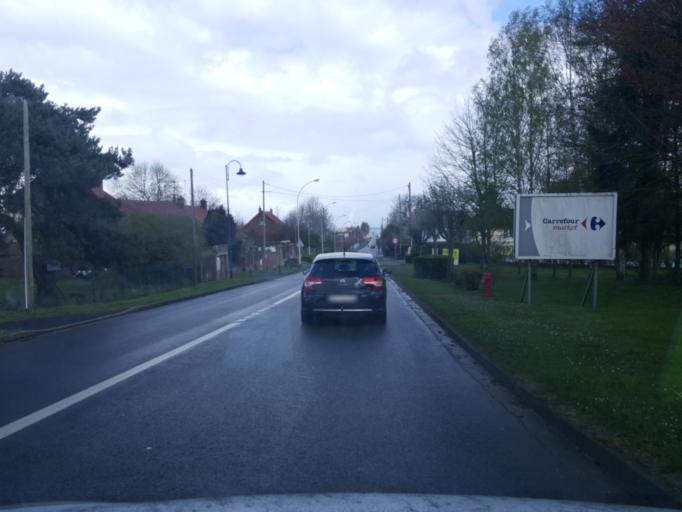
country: FR
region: Picardie
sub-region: Departement de l'Oise
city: Auneuil
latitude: 49.3681
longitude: 1.9861
